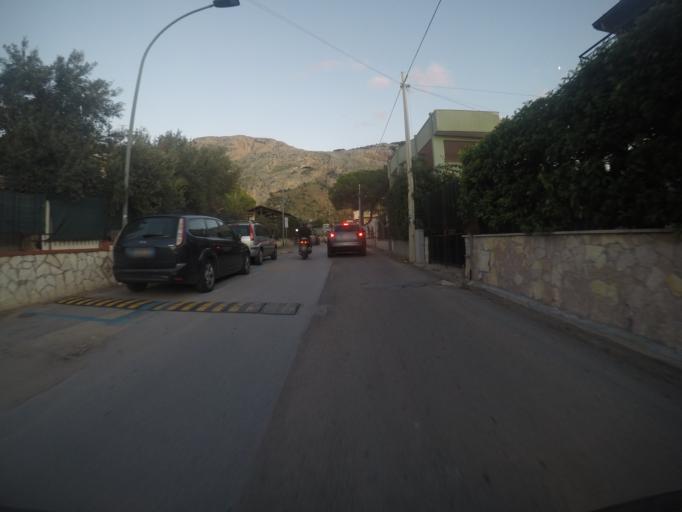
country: IT
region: Sicily
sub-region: Palermo
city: Isola delle Femmine
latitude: 38.1853
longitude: 13.2407
